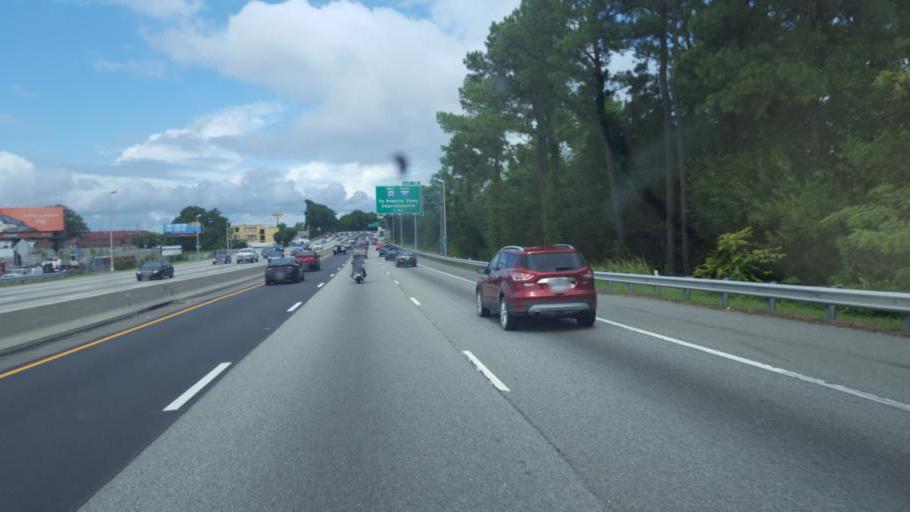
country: US
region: Virginia
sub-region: City of Richmond
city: Richmond
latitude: 37.5723
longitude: -77.4562
